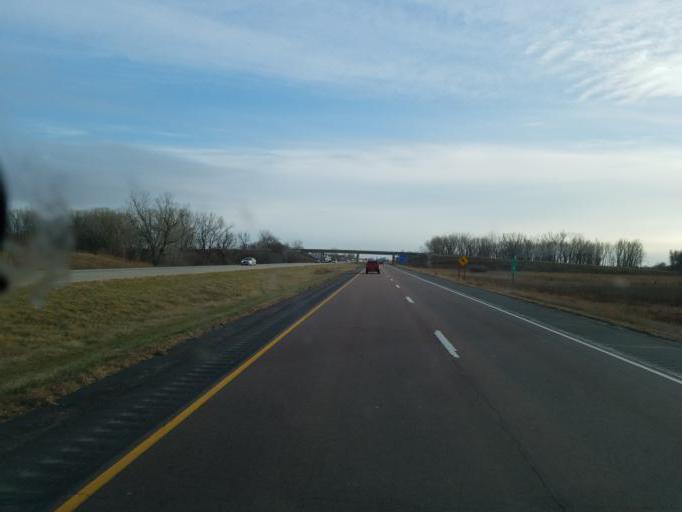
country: US
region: Iowa
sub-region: Woodbury County
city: Sergeant Bluff
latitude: 42.3840
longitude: -96.3600
